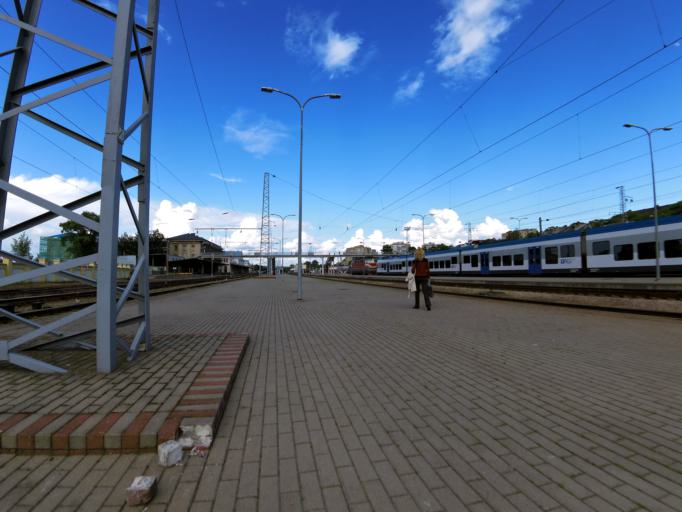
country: LT
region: Vilnius County
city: Naujamiestis
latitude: 54.6686
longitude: 25.2809
